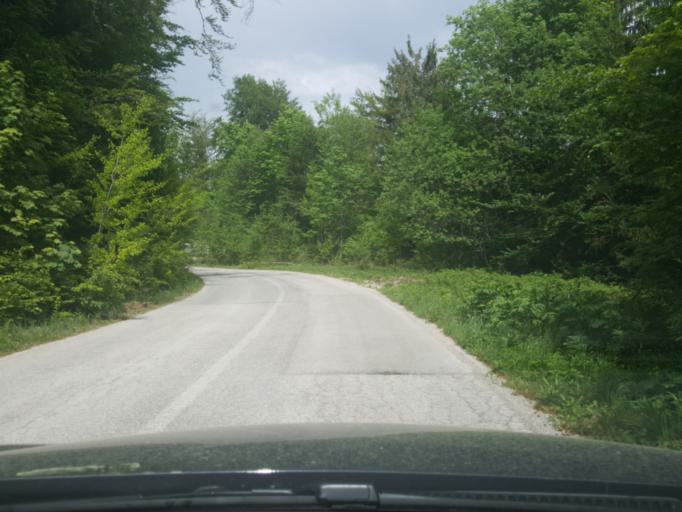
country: RS
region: Central Serbia
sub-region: Zlatiborski Okrug
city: Bajina Basta
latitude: 43.9121
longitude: 19.5027
